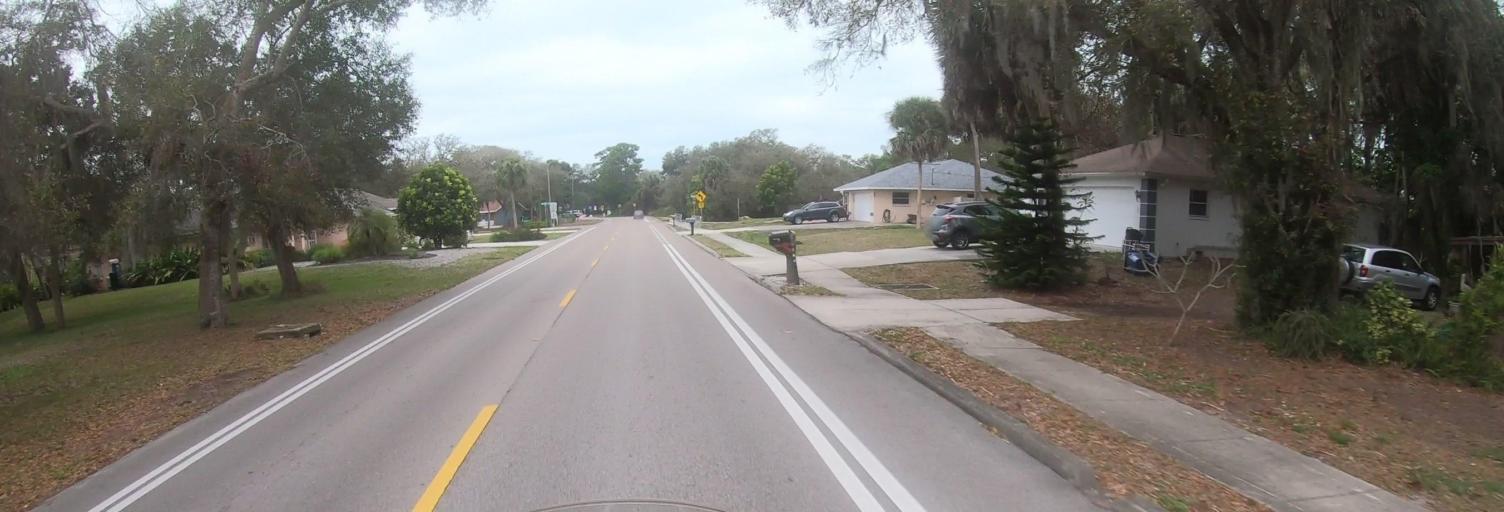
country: US
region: Florida
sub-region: Sarasota County
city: South Venice
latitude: 27.0702
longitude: -82.4276
